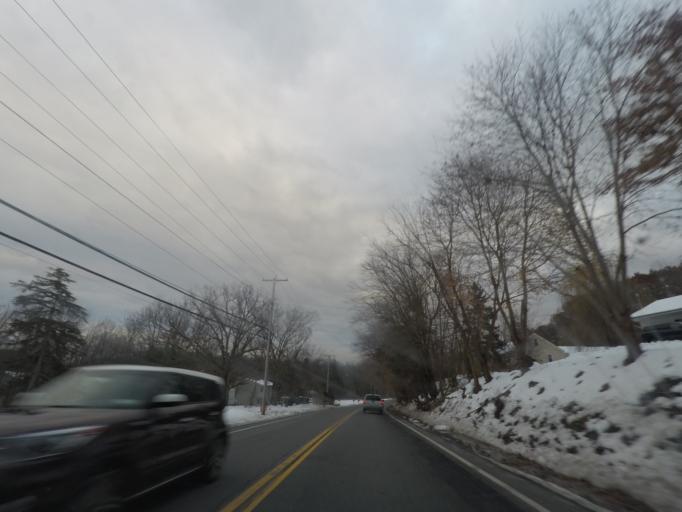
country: US
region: New York
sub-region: Orange County
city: Gardnertown
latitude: 41.5404
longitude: -74.0434
